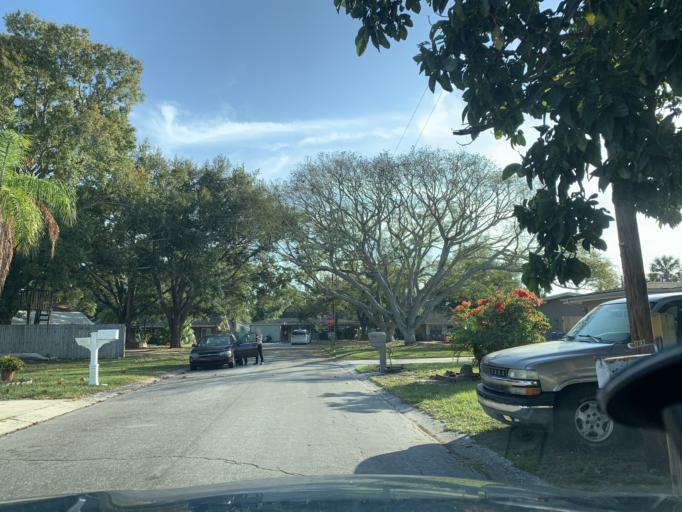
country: US
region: Florida
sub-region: Pinellas County
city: Ridgecrest
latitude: 27.9003
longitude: -82.7970
